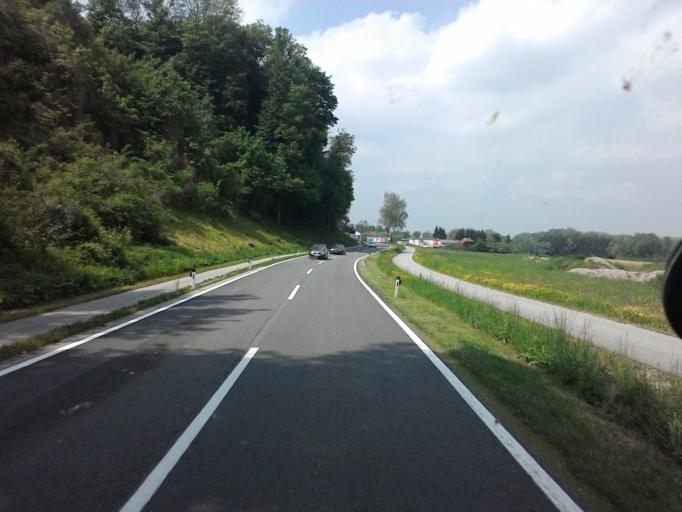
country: AT
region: Upper Austria
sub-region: Politischer Bezirk Steyr-Land
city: Bad Hall
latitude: 48.0509
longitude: 14.2038
